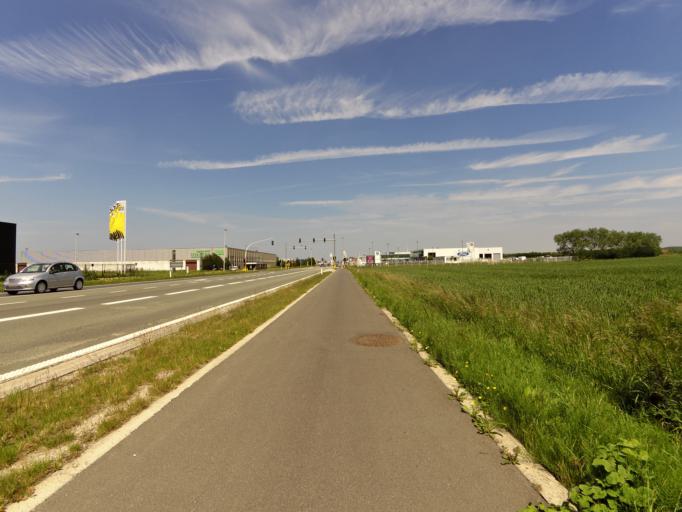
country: BE
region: Flanders
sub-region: Provincie West-Vlaanderen
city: Ostend
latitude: 51.1921
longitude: 2.9007
